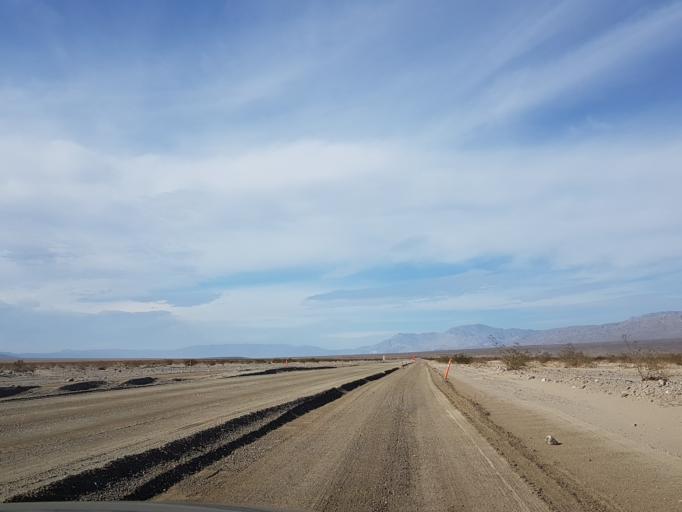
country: US
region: California
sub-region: San Bernardino County
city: Searles Valley
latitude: 36.1484
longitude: -117.2973
